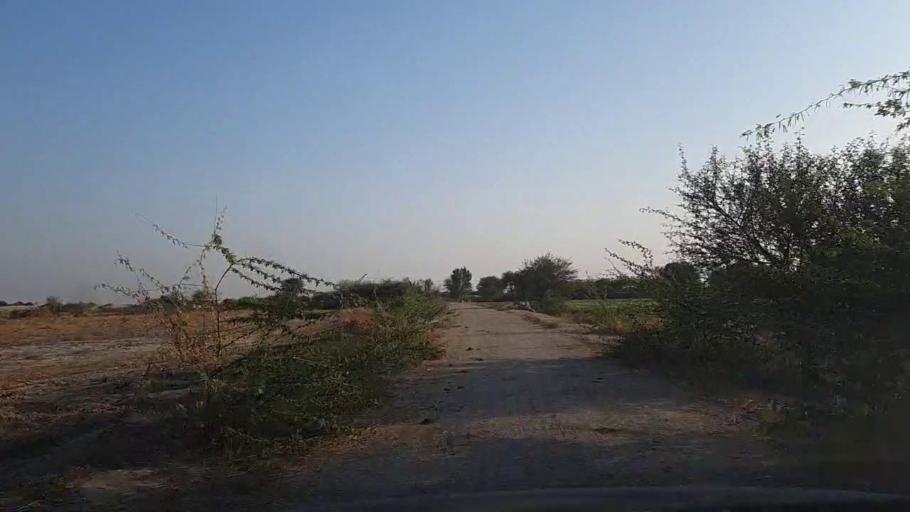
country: PK
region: Sindh
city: Naukot
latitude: 24.8933
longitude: 69.3454
